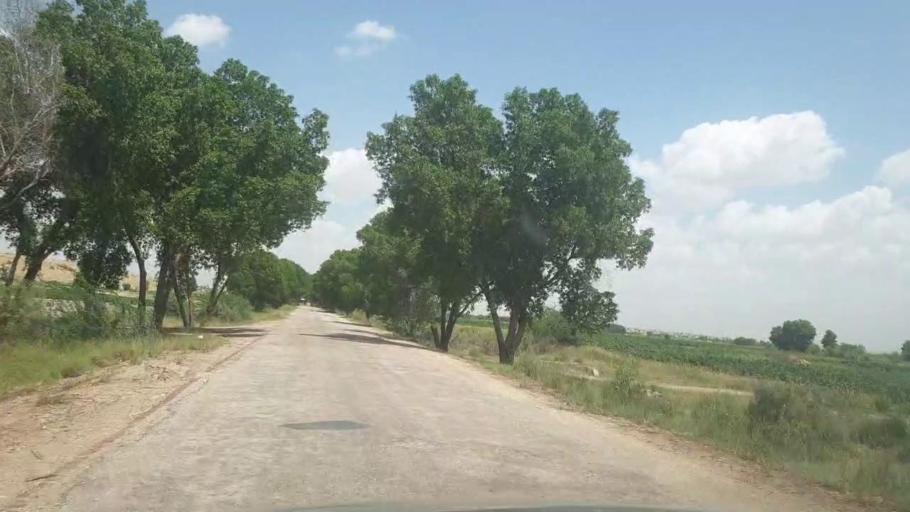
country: PK
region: Sindh
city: Kot Diji
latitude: 27.2199
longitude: 69.0461
